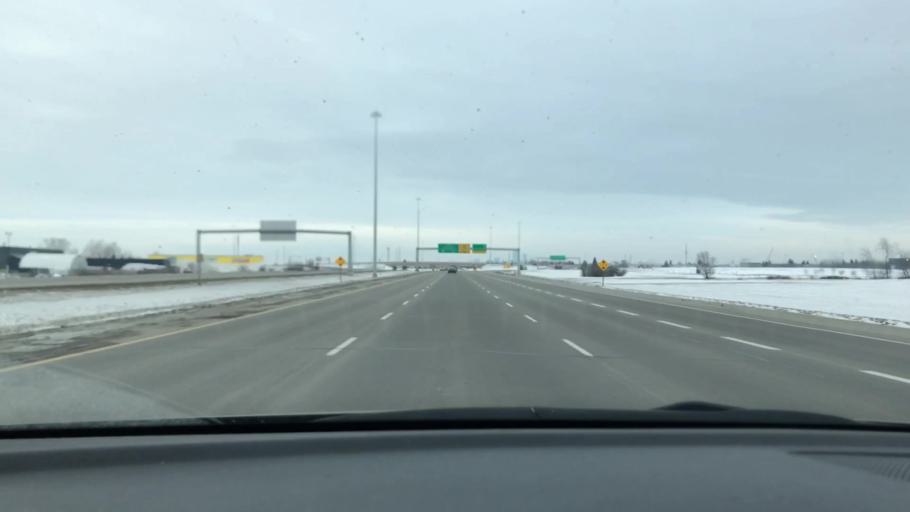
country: CA
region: Alberta
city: Sherwood Park
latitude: 53.5155
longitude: -113.3583
